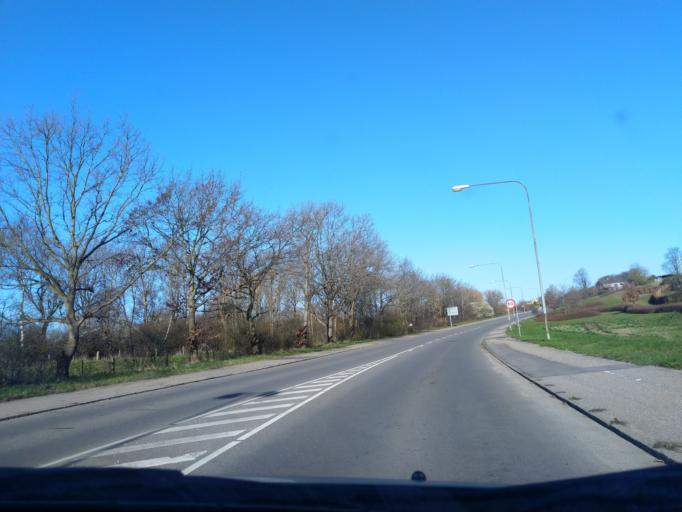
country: DK
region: Zealand
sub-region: Kalundborg Kommune
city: Kalundborg
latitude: 55.6883
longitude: 11.0567
